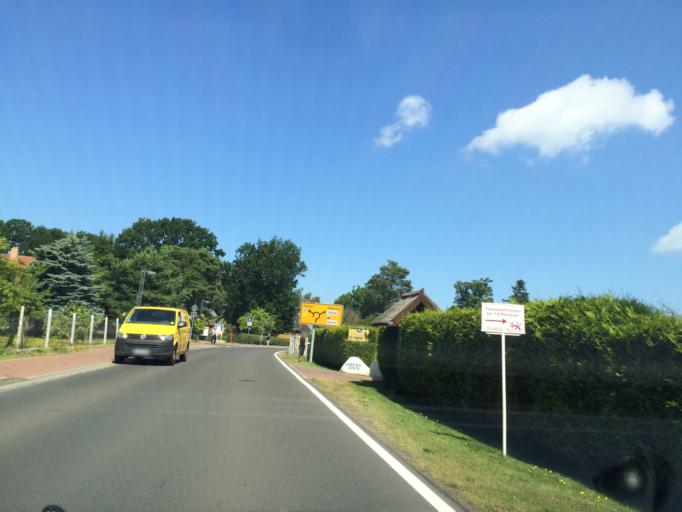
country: DE
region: Mecklenburg-Vorpommern
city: Zingst
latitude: 54.4308
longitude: 12.6806
